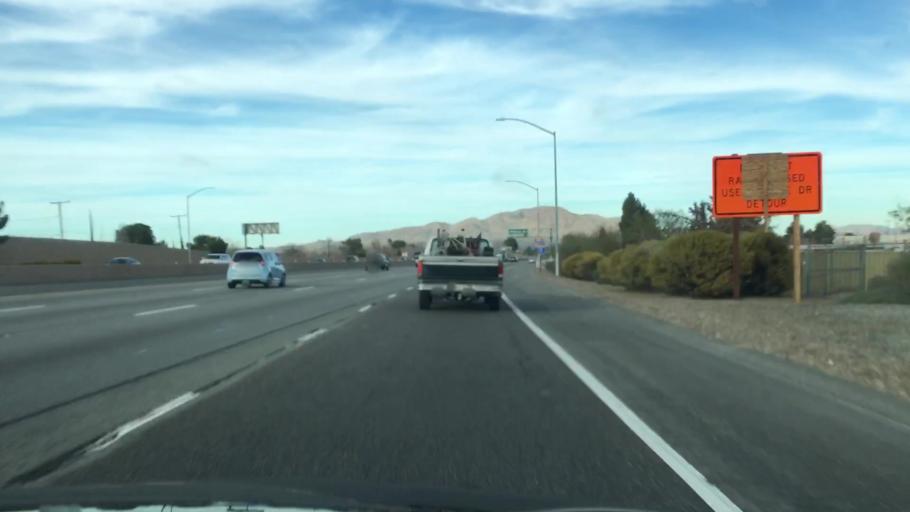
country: US
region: California
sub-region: San Bernardino County
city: Victorville
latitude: 34.5214
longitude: -117.3190
